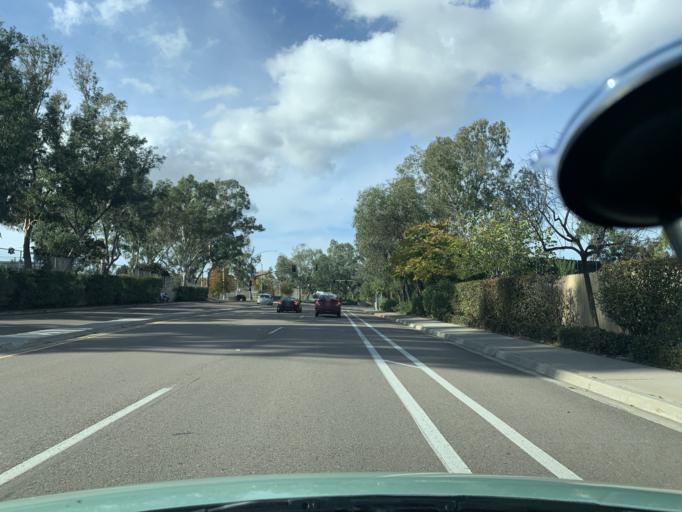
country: US
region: California
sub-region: San Diego County
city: San Diego
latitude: 32.7933
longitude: -117.1692
